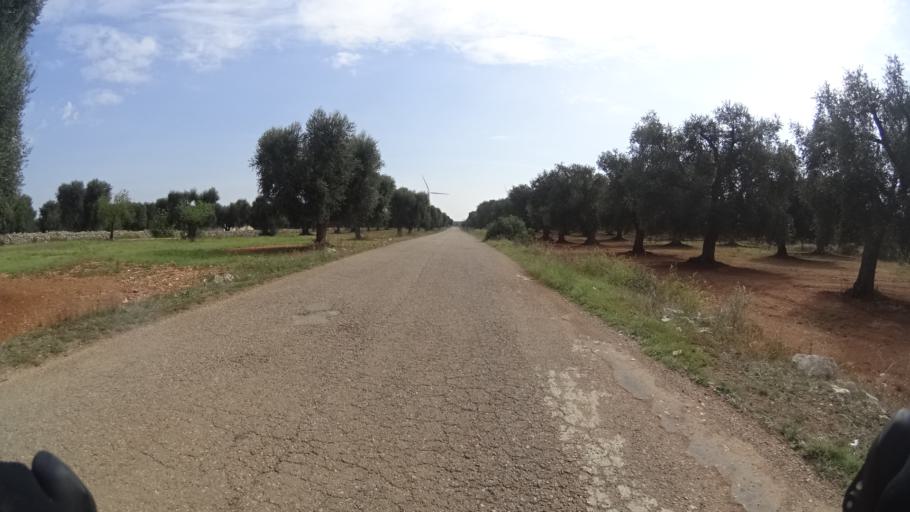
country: IT
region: Apulia
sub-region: Provincia di Taranto
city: San Marzano di San Giuseppe
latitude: 40.4382
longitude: 17.5325
